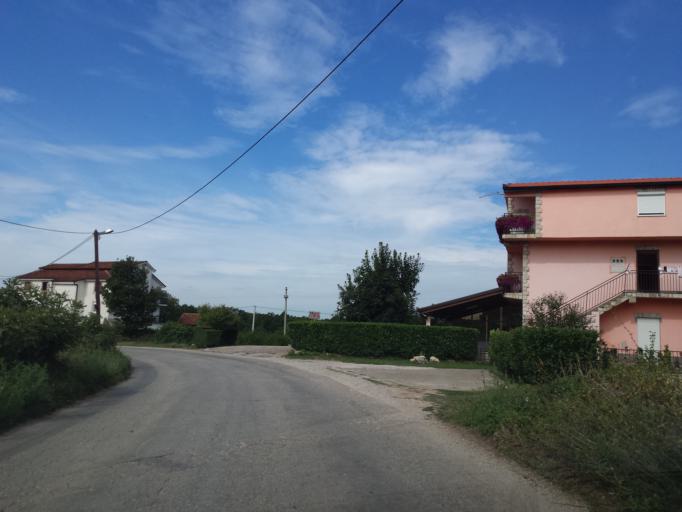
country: BA
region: Federation of Bosnia and Herzegovina
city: Citluk
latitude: 43.1980
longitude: 17.6653
